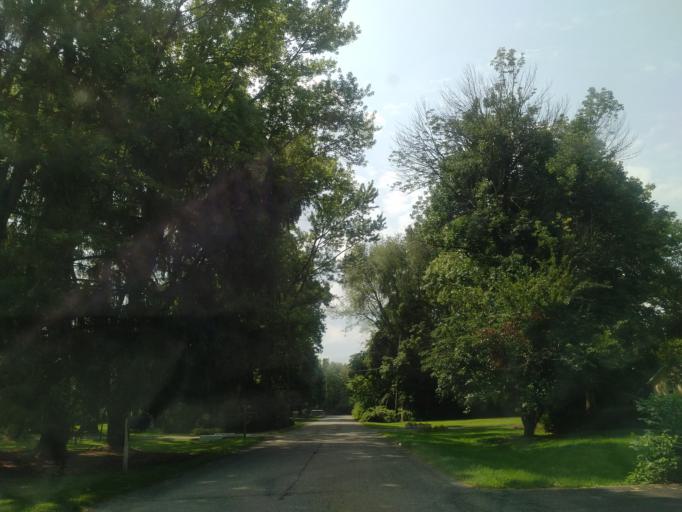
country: US
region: Indiana
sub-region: Marion County
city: Meridian Hills
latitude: 39.9143
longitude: -86.1257
